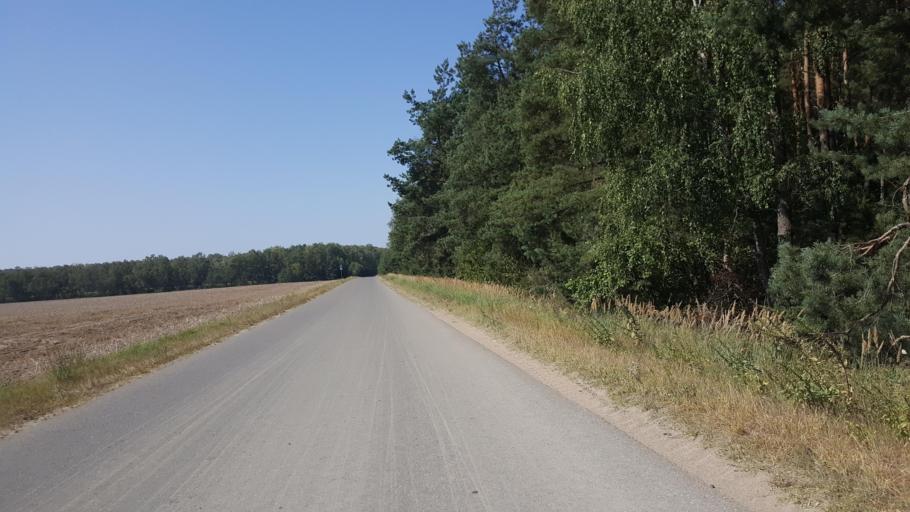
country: BY
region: Brest
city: Vysokaye
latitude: 52.4281
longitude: 23.4533
